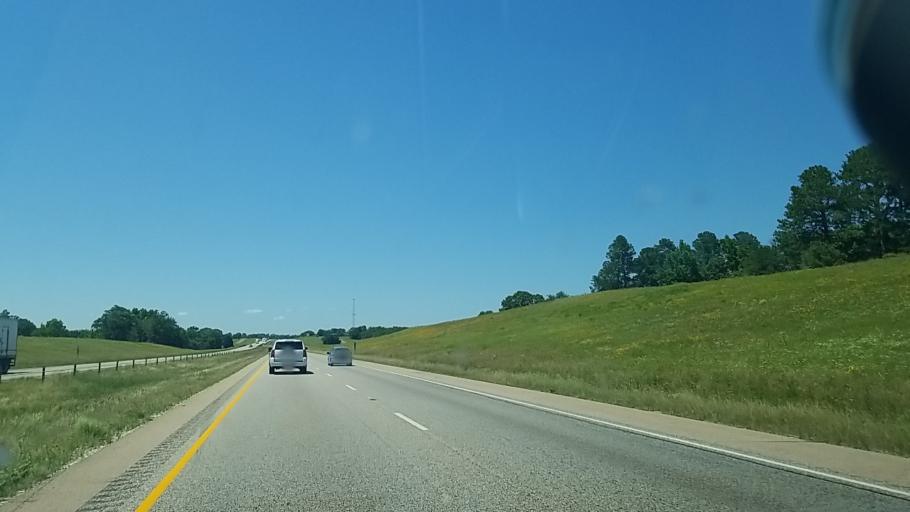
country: US
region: Texas
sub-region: Leon County
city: Buffalo
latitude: 31.4071
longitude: -96.0395
